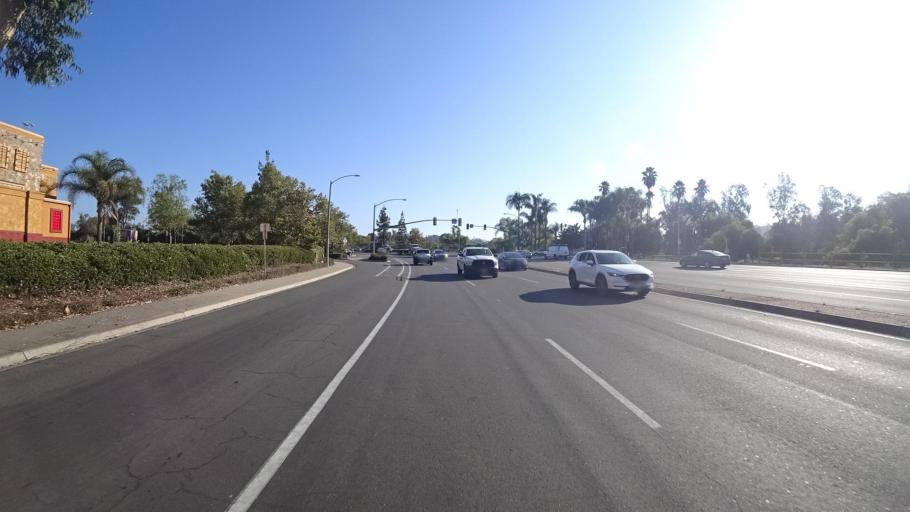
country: US
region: California
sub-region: San Diego County
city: Escondido
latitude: 33.0688
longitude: -117.0614
